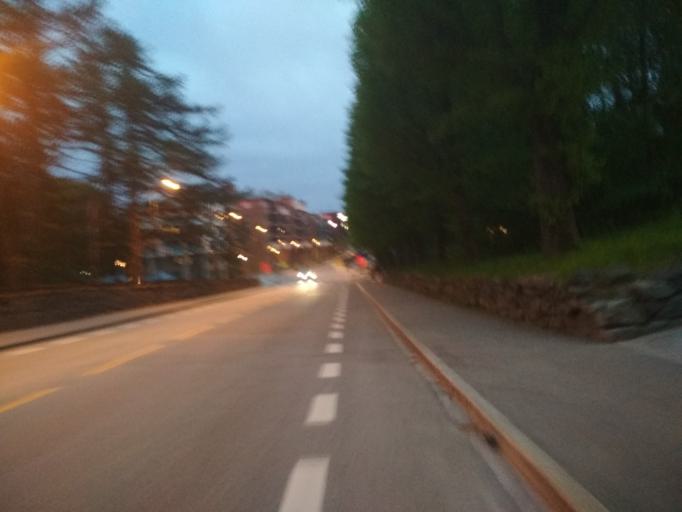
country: NO
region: Rogaland
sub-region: Stavanger
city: Stavanger
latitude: 58.9760
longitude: 5.7184
